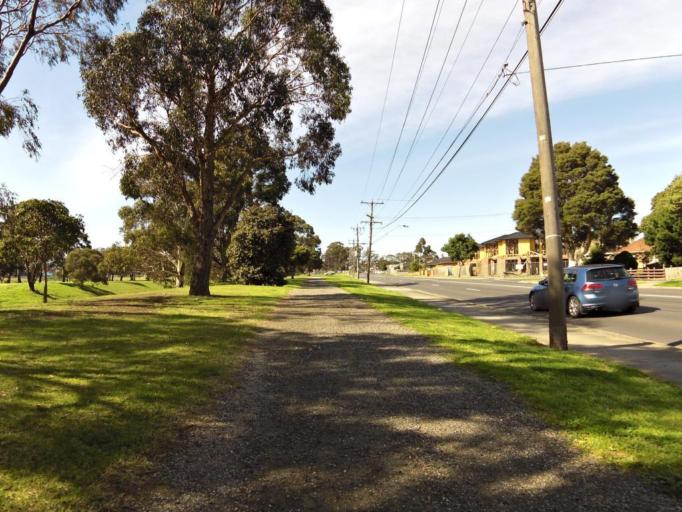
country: AU
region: Victoria
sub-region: Greater Dandenong
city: Dandenong
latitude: -37.9938
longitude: 145.2114
